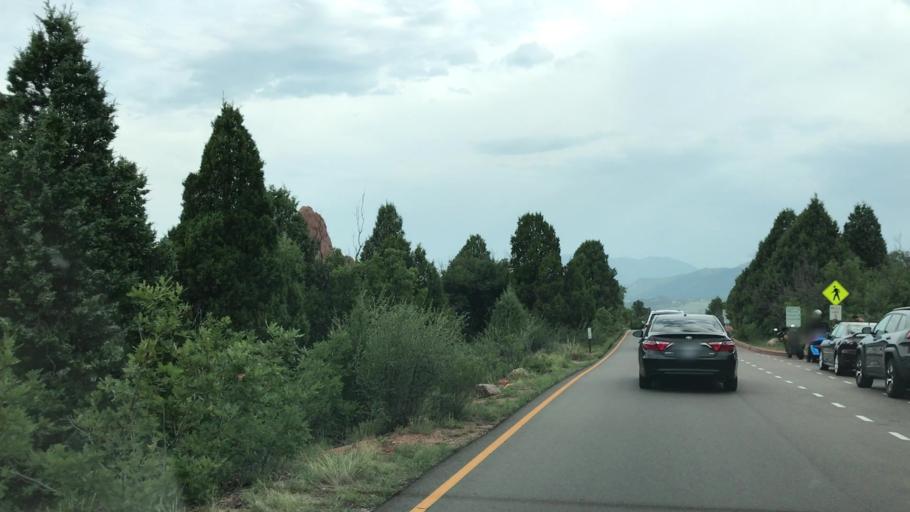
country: US
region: Colorado
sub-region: El Paso County
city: Manitou Springs
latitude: 38.8781
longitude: -104.8833
